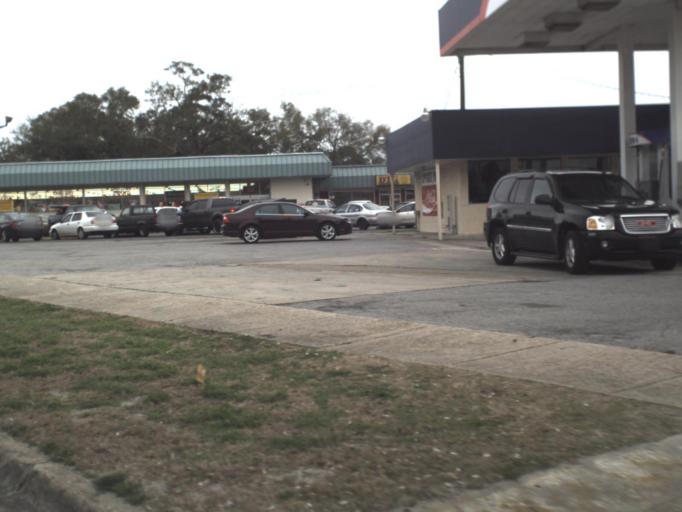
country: US
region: Florida
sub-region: Bay County
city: Pretty Bayou
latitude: 30.1770
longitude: -85.7010
